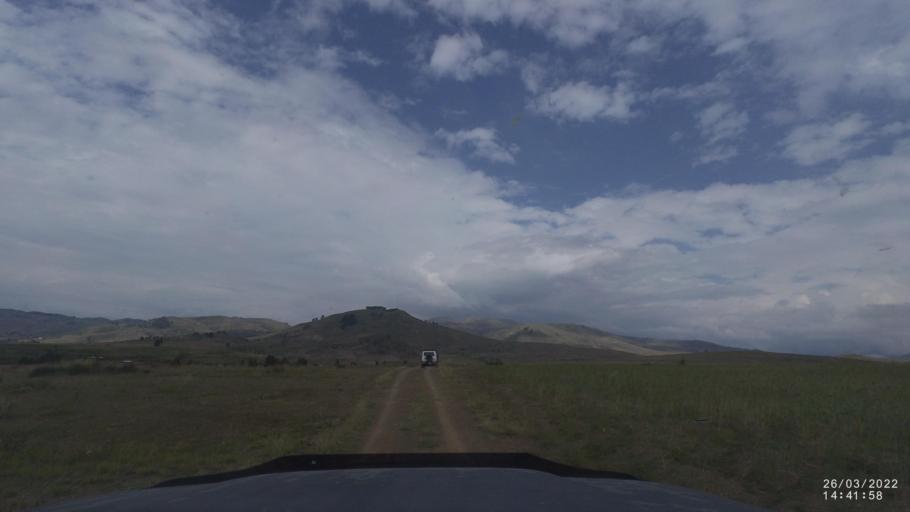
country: BO
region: Cochabamba
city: Cliza
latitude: -17.7374
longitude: -65.8555
